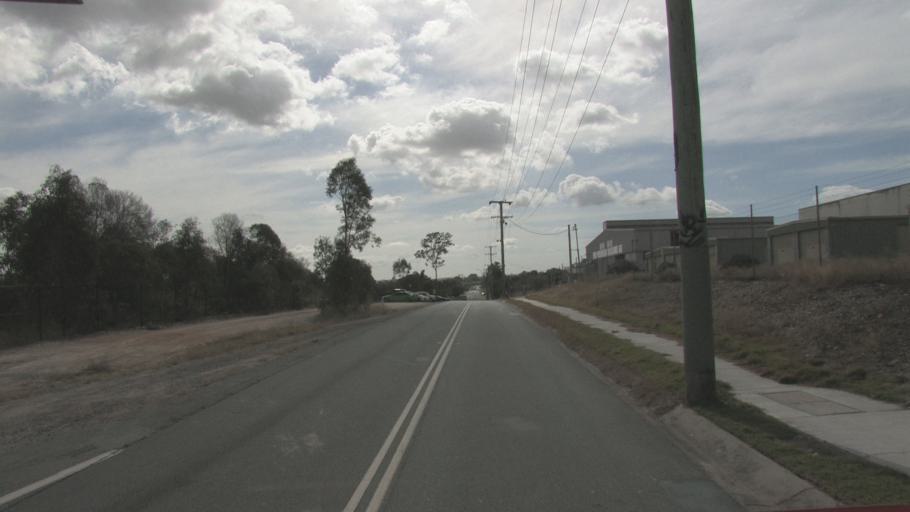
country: AU
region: Queensland
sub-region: Logan
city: Waterford West
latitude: -27.7040
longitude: 153.1545
